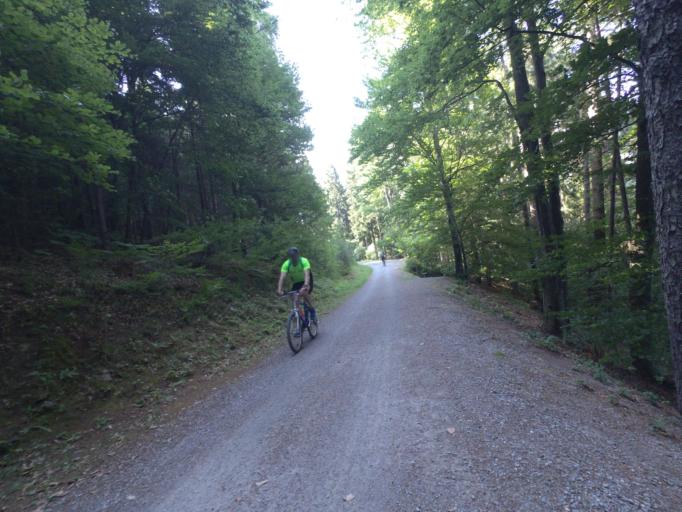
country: AT
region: Carinthia
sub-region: Politischer Bezirk Spittal an der Drau
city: Millstatt
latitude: 46.7826
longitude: 13.5932
